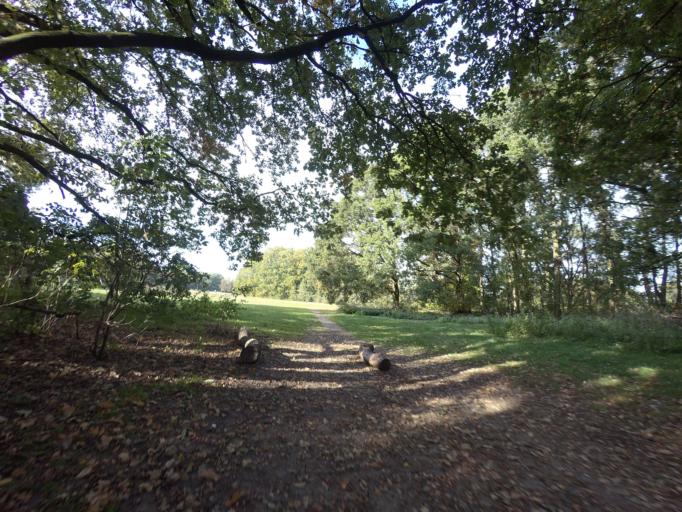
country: BE
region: Flanders
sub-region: Provincie Antwerpen
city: Schoten
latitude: 51.2324
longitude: 4.4807
